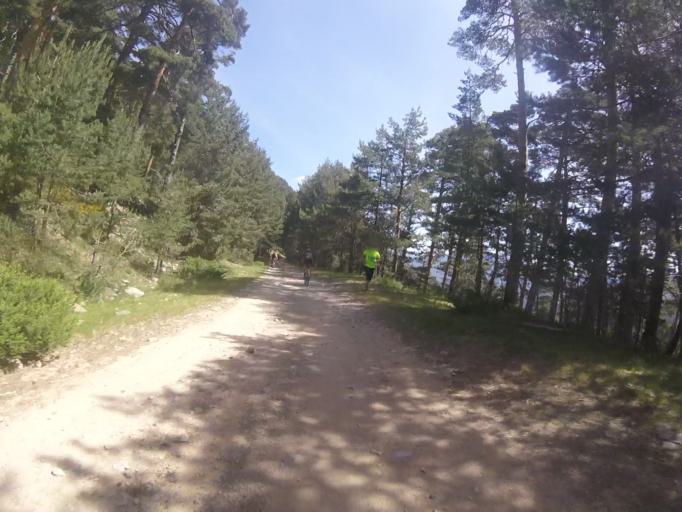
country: ES
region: Madrid
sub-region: Provincia de Madrid
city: Cercedilla
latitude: 40.7976
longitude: -4.0619
